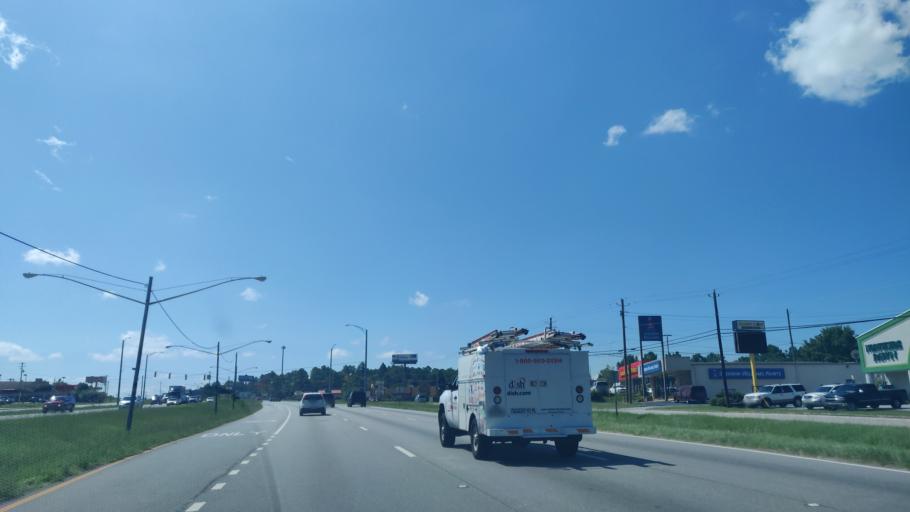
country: US
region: Alabama
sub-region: Russell County
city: Phenix City
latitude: 32.4677
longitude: -85.0281
